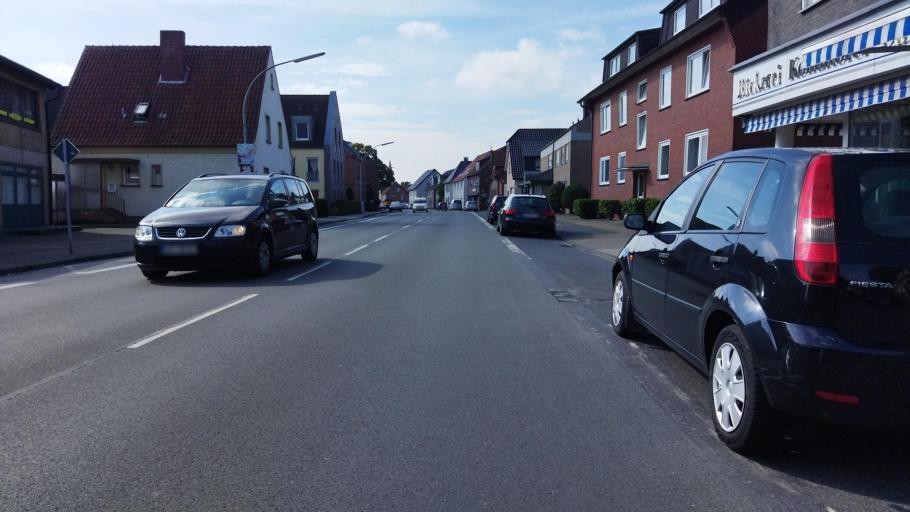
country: DE
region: North Rhine-Westphalia
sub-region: Regierungsbezirk Munster
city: Warendorf
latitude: 51.9594
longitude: 7.9933
